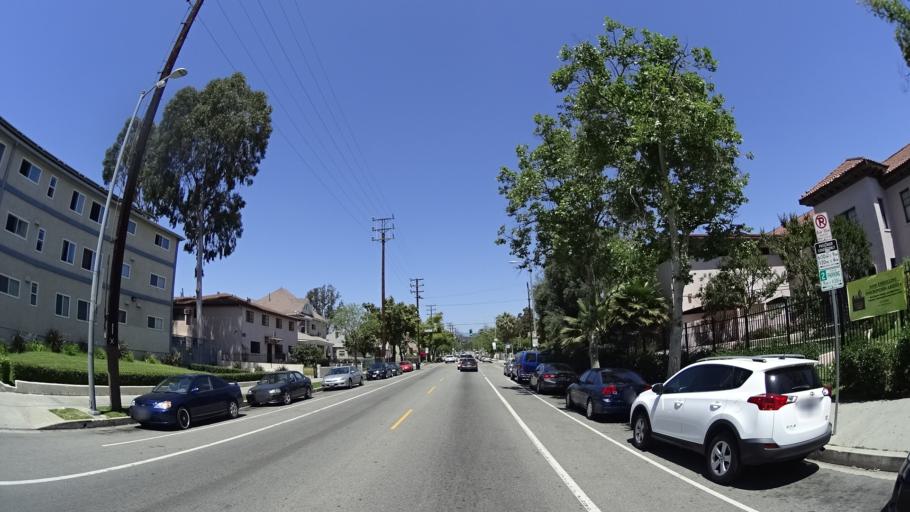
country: US
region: California
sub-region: Los Angeles County
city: Los Angeles
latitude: 34.0785
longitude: -118.2119
